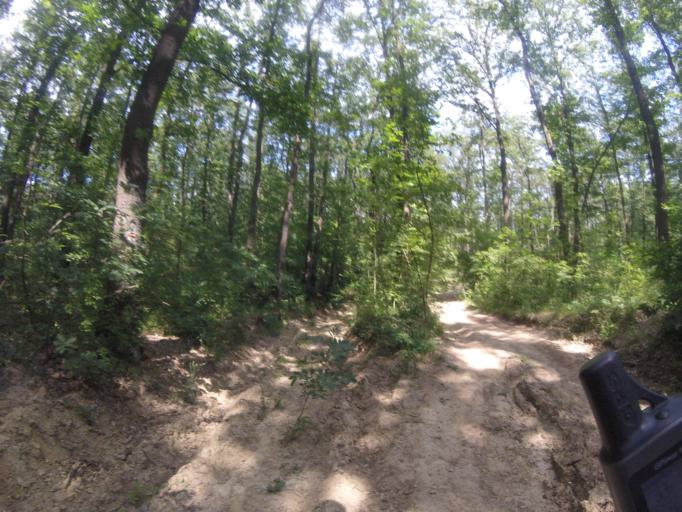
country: HU
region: Fejer
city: Szarliget
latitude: 47.4871
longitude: 18.4891
